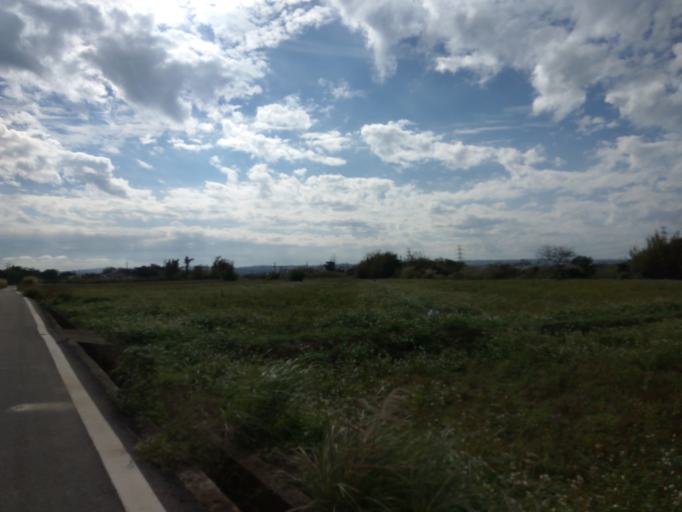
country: TW
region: Taiwan
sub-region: Hsinchu
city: Zhubei
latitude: 24.9588
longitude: 121.1041
